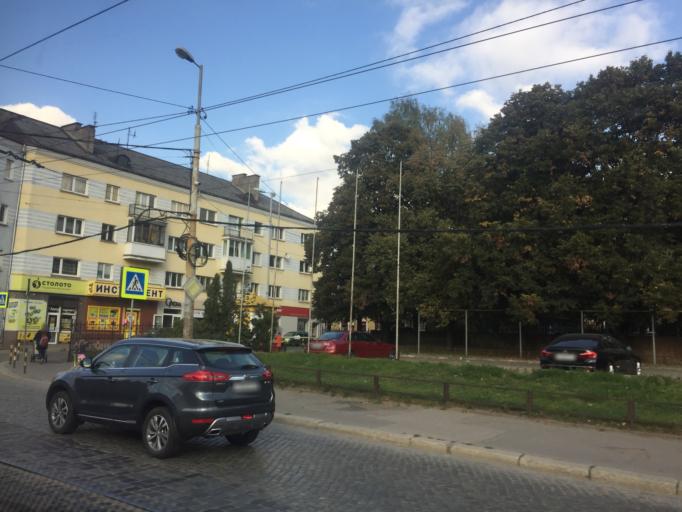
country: RU
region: Kaliningrad
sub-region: Gorod Kaliningrad
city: Kaliningrad
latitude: 54.6967
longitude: 20.5031
